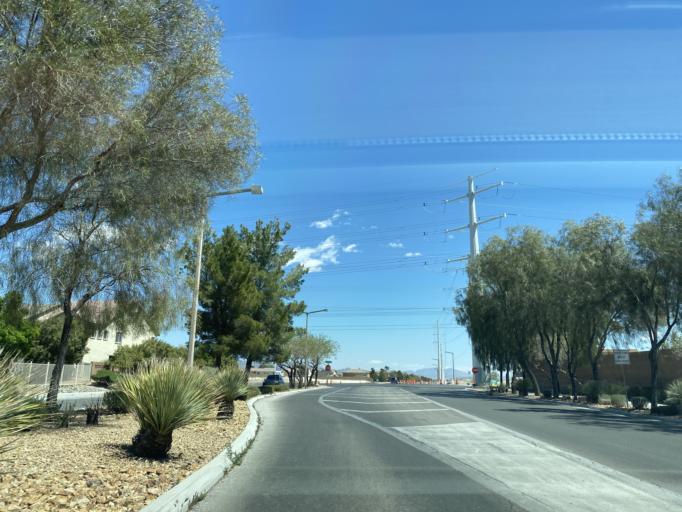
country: US
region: Nevada
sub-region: Clark County
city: North Las Vegas
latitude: 36.3060
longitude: -115.2084
